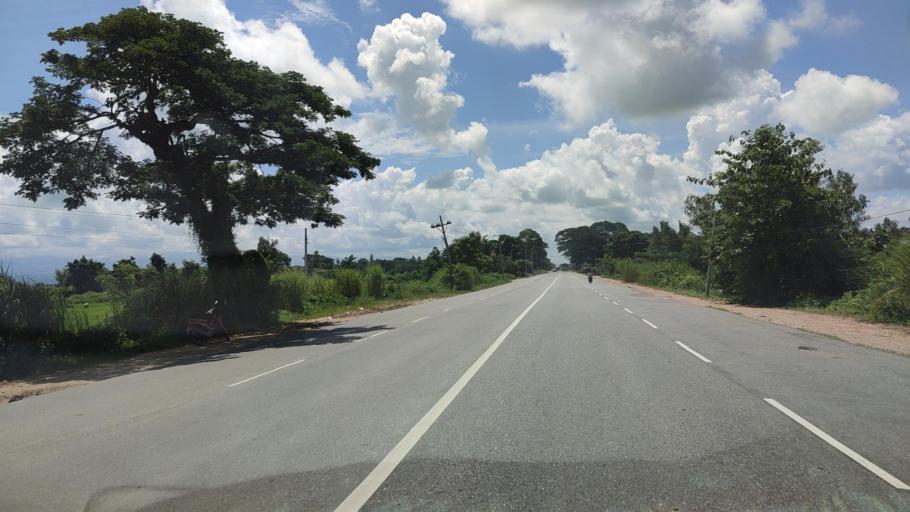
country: MM
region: Bago
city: Taungoo
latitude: 19.1745
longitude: 96.3316
